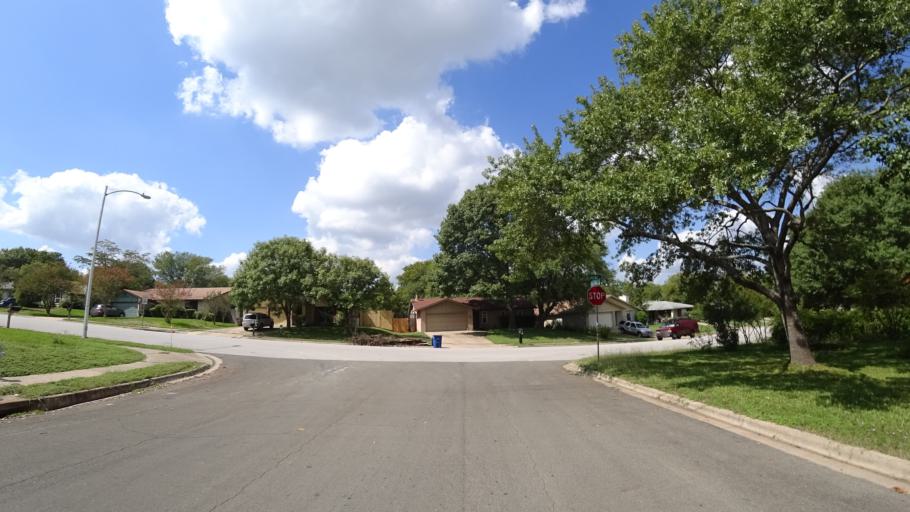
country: US
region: Texas
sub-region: Travis County
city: Onion Creek
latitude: 30.1930
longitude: -97.7833
